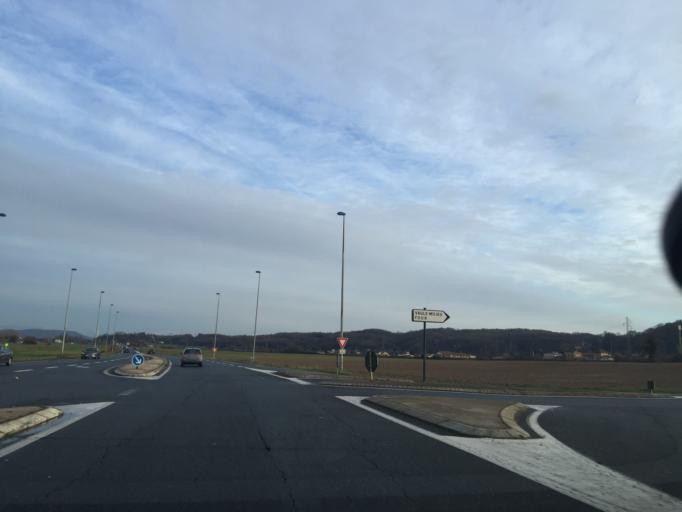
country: FR
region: Rhone-Alpes
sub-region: Departement de l'Isere
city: Vaulx-Milieu
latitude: 45.6183
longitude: 5.1838
